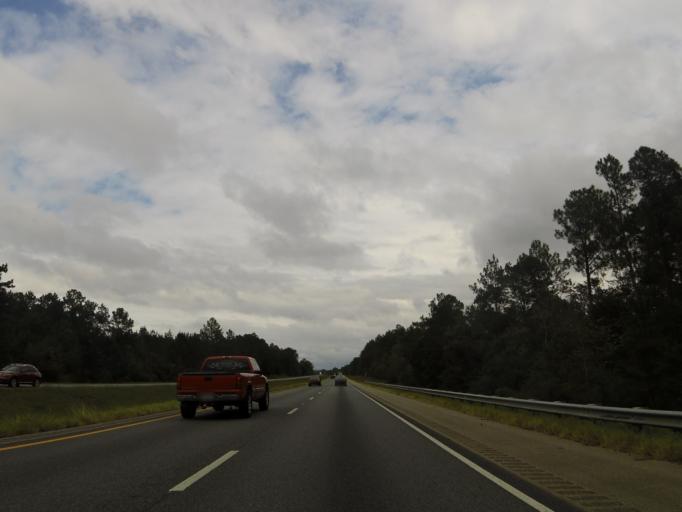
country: US
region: Alabama
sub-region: Escambia County
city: Brewton
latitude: 31.2441
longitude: -87.2504
